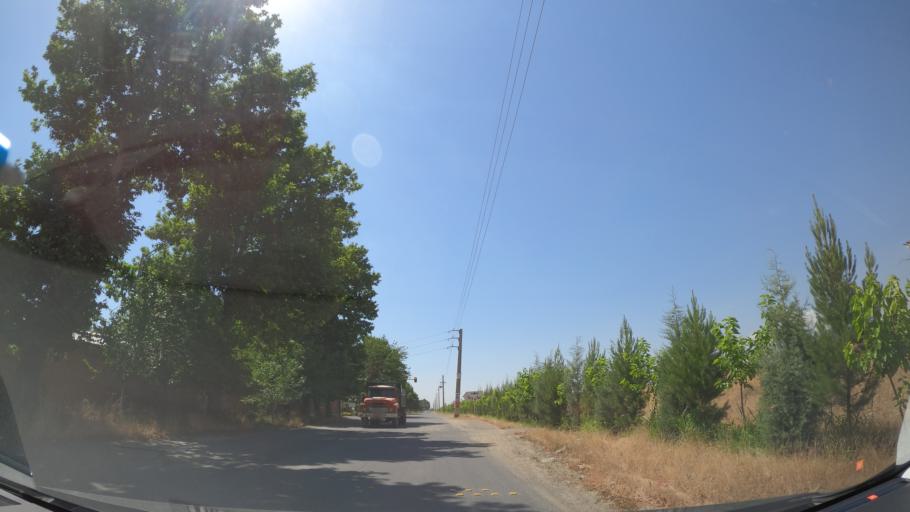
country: IR
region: Alborz
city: Hashtgerd
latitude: 35.9168
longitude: 50.7306
